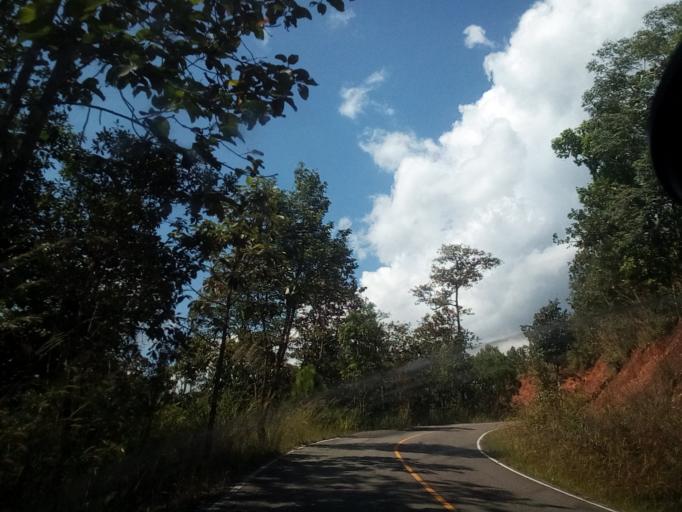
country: TH
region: Chiang Mai
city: Samoeng
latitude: 18.8762
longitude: 98.6819
